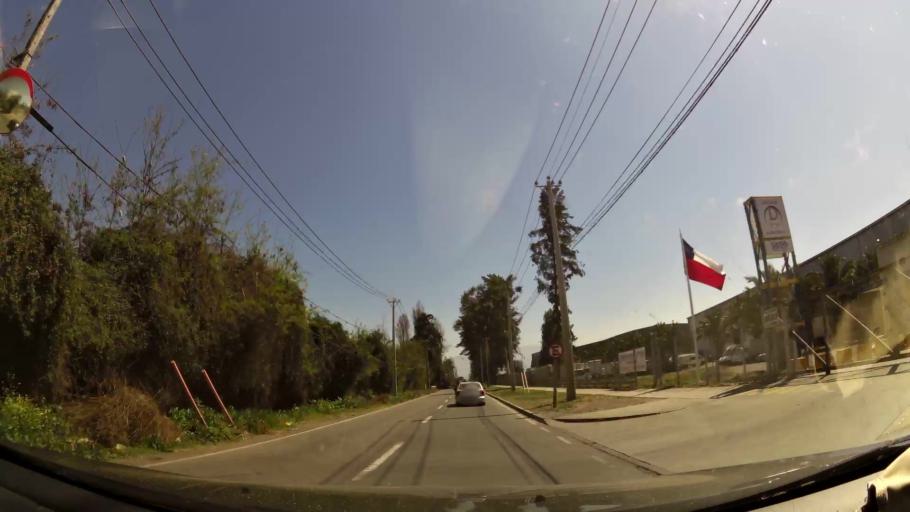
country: CL
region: Santiago Metropolitan
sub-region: Provincia de Santiago
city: Lo Prado
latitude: -33.3907
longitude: -70.7789
